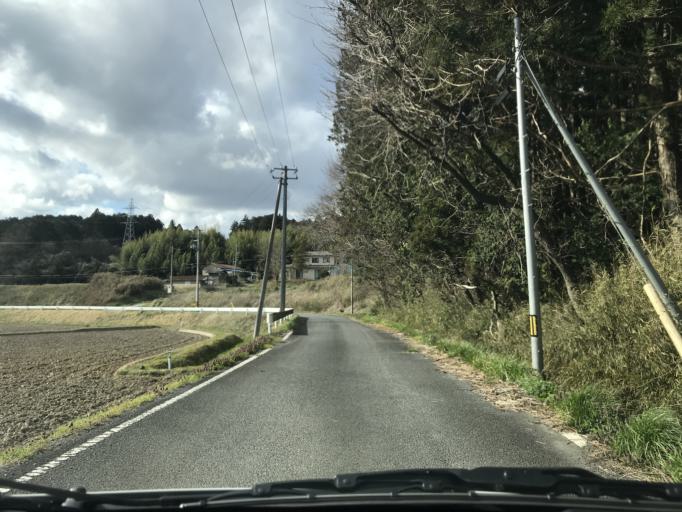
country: JP
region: Miyagi
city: Wakuya
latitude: 38.6110
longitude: 141.2334
